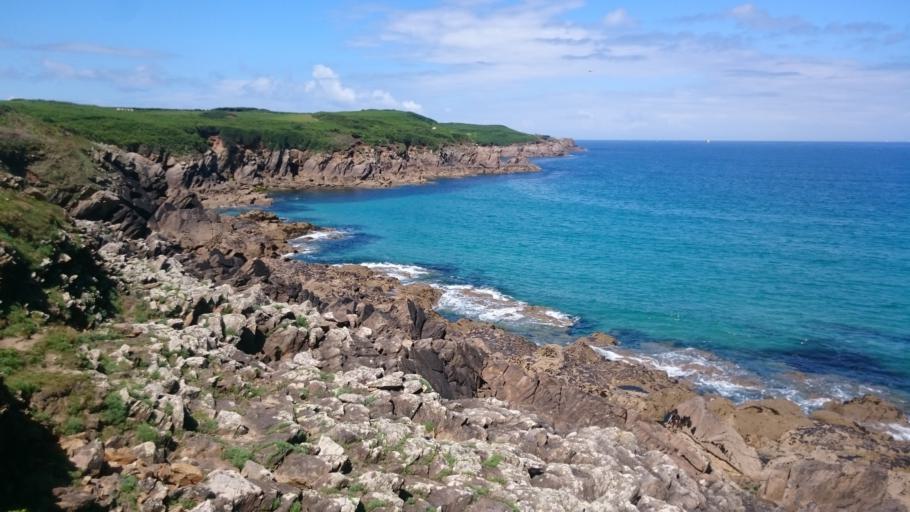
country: FR
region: Brittany
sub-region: Departement du Finistere
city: Le Conquet
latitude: 48.3643
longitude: -4.7768
